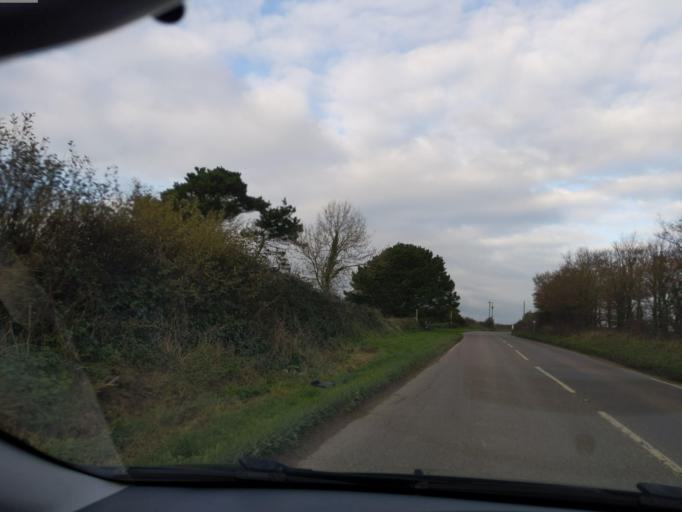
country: GB
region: England
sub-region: Cornwall
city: Padstow
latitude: 50.5303
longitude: -4.9520
